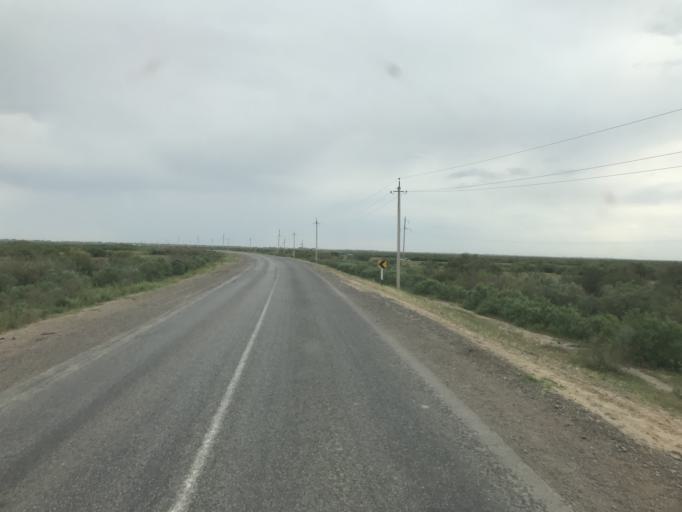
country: KZ
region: Ongtustik Qazaqstan
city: Asykata
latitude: 41.0055
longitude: 68.4737
